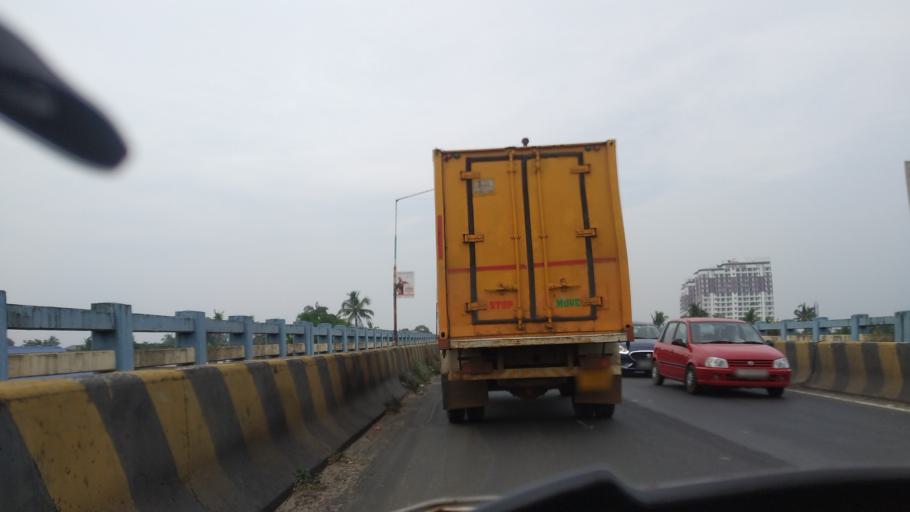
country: IN
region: Kerala
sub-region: Ernakulam
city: Elur
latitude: 10.0342
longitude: 76.3036
